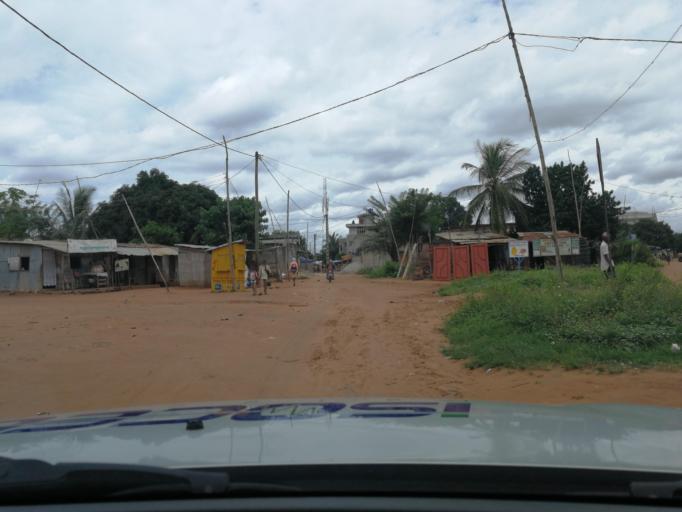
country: BJ
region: Atlantique
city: Abomey-Calavi
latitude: 6.4362
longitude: 2.3059
